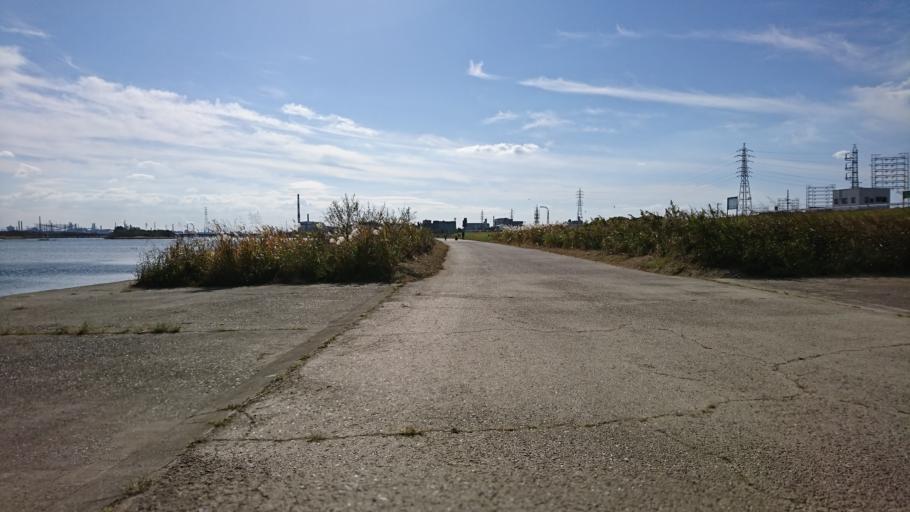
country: JP
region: Hyogo
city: Kakogawacho-honmachi
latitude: 34.7616
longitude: 134.8062
